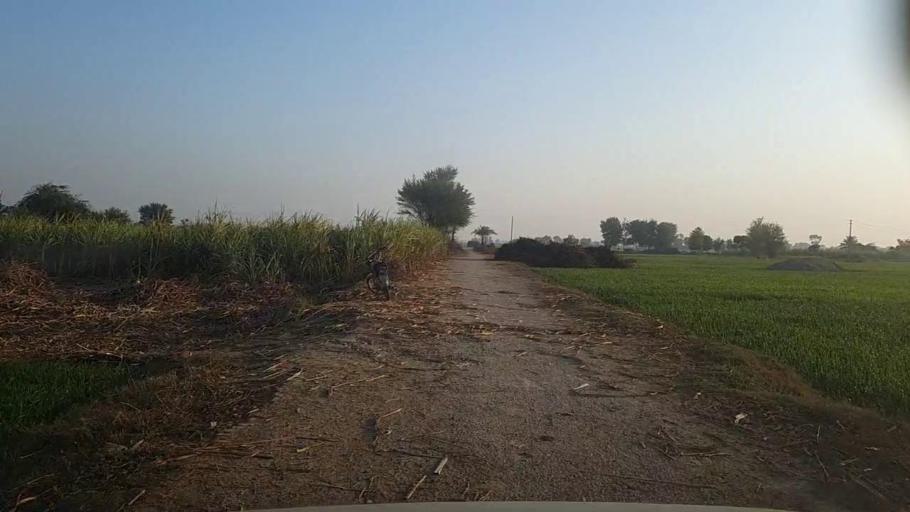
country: PK
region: Sindh
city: Khairpur
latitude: 28.0564
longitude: 69.7584
